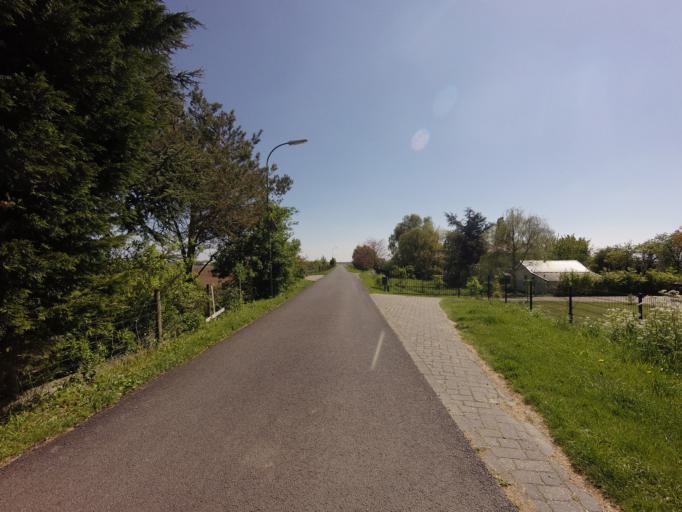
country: NL
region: South Holland
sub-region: Gemeente Dordrecht
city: Dordrecht
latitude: 51.7661
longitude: 4.6564
